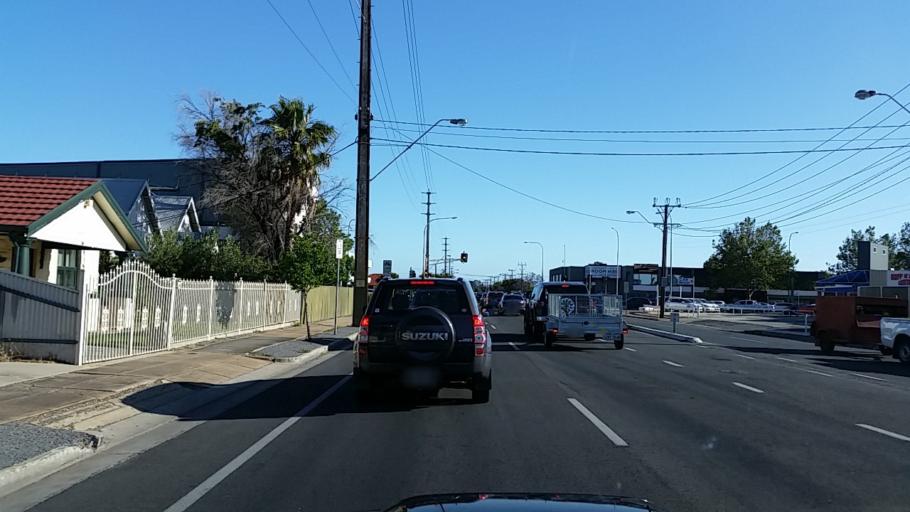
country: AU
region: South Australia
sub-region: City of West Torrens
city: Plympton
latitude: -34.9318
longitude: 138.5525
